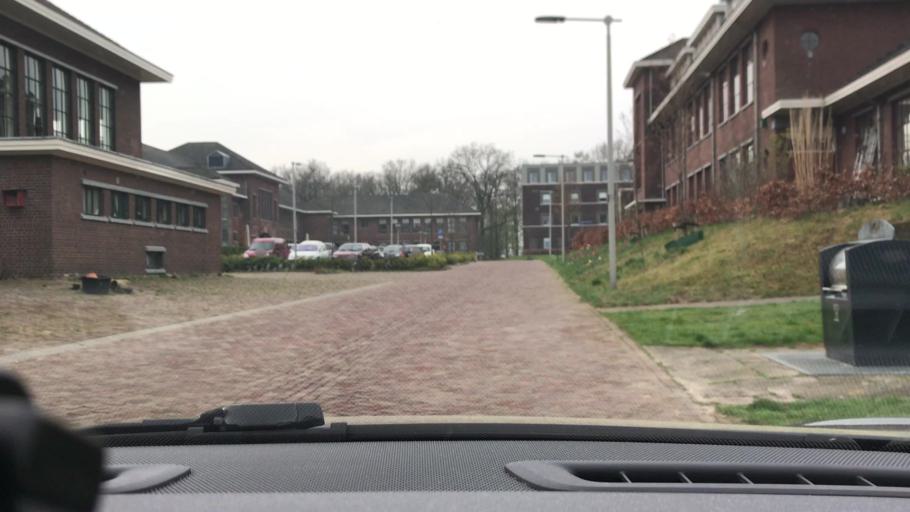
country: NL
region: Gelderland
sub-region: Gemeente Arnhem
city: Arnhem
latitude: 52.0029
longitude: 5.9283
